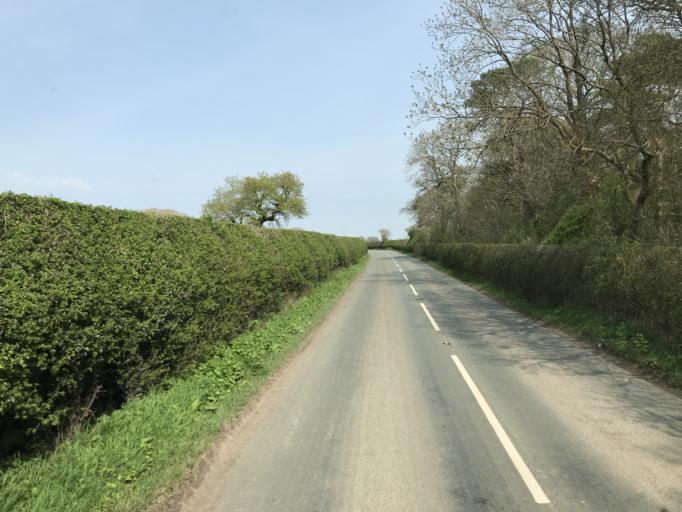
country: GB
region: England
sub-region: Cheshire West and Chester
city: Aldford
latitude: 53.1423
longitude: -2.8632
